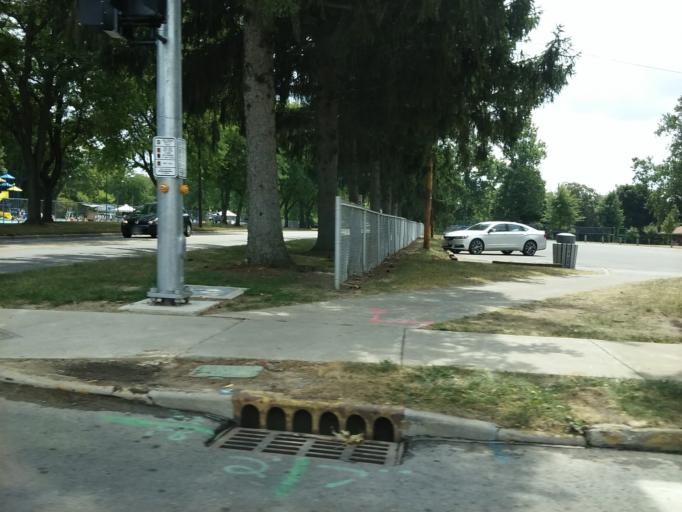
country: US
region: Ohio
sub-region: Hancock County
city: Findlay
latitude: 41.0439
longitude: -83.6328
